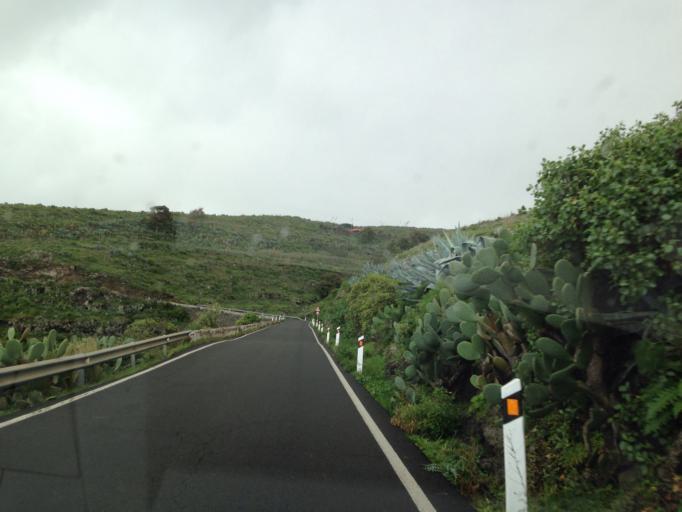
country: ES
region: Canary Islands
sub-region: Provincia de Las Palmas
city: Guia
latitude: 28.1164
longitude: -15.6450
